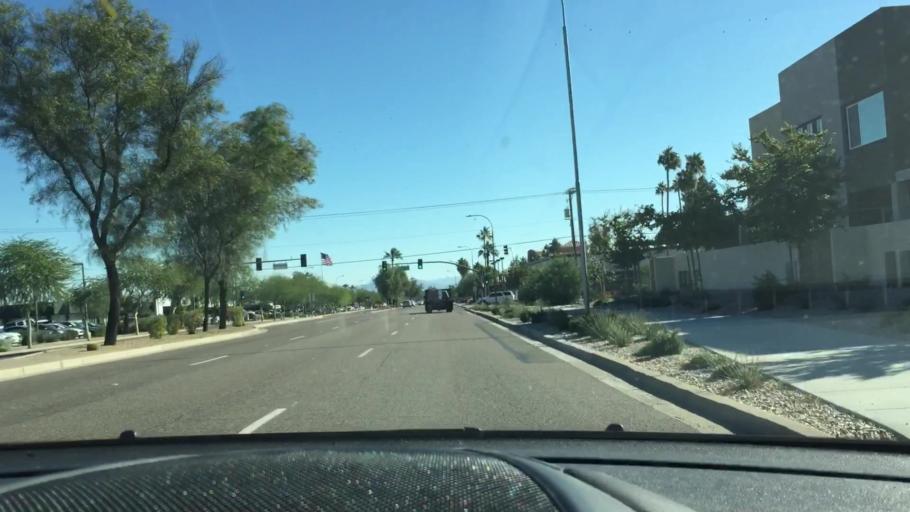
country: US
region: Arizona
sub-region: Maricopa County
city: Tempe Junction
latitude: 33.4656
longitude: -111.9316
